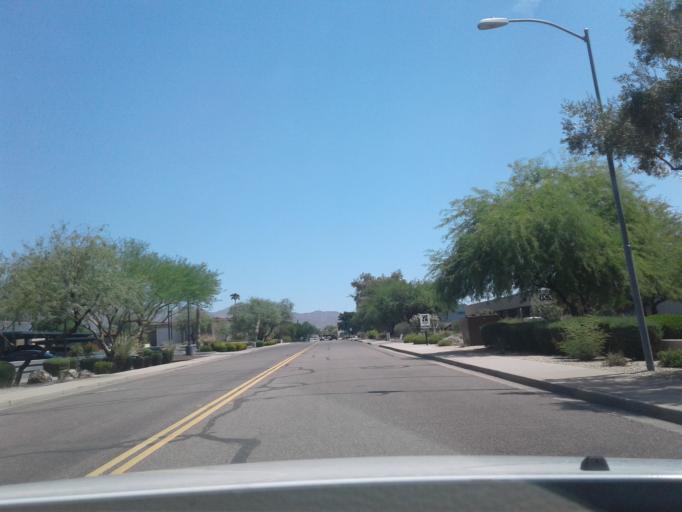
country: US
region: Arizona
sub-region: Maricopa County
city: Paradise Valley
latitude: 33.6177
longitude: -111.9126
